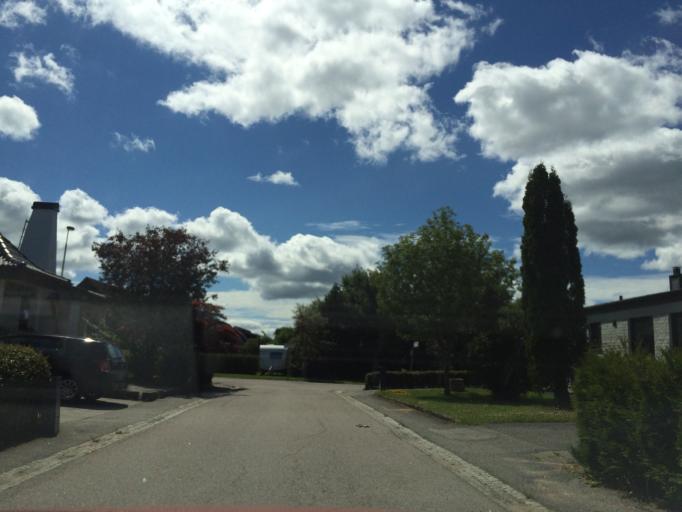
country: SE
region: Vaestra Goetaland
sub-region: Trollhattan
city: Trollhattan
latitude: 58.2857
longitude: 12.3262
